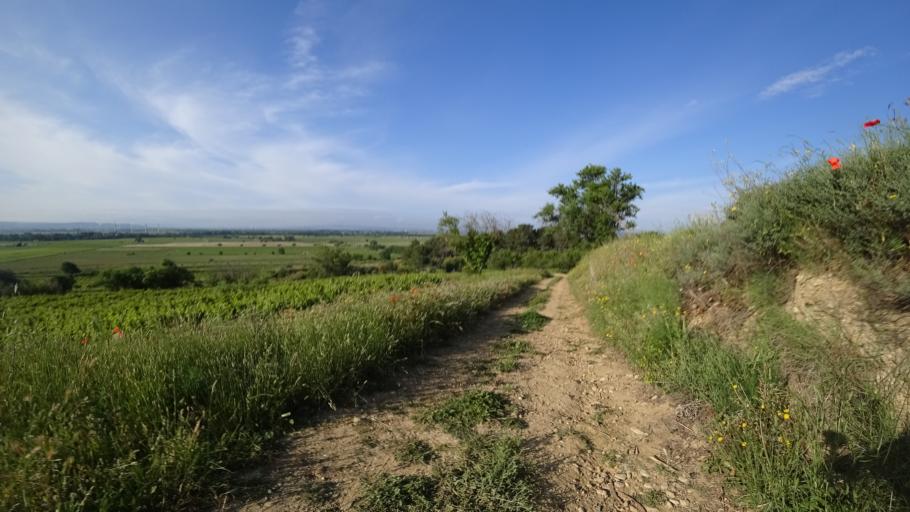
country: FR
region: Languedoc-Roussillon
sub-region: Departement de l'Aude
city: Canet
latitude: 43.2539
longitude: 2.8137
